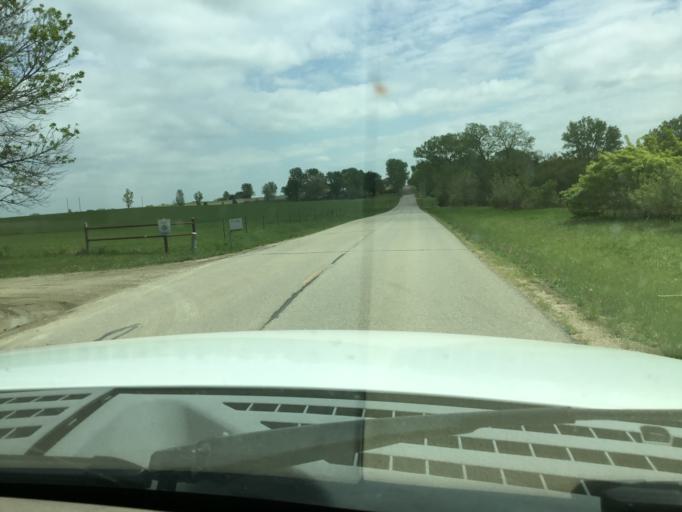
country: US
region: Kansas
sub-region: Shawnee County
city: Auburn
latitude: 38.9707
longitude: -95.8030
